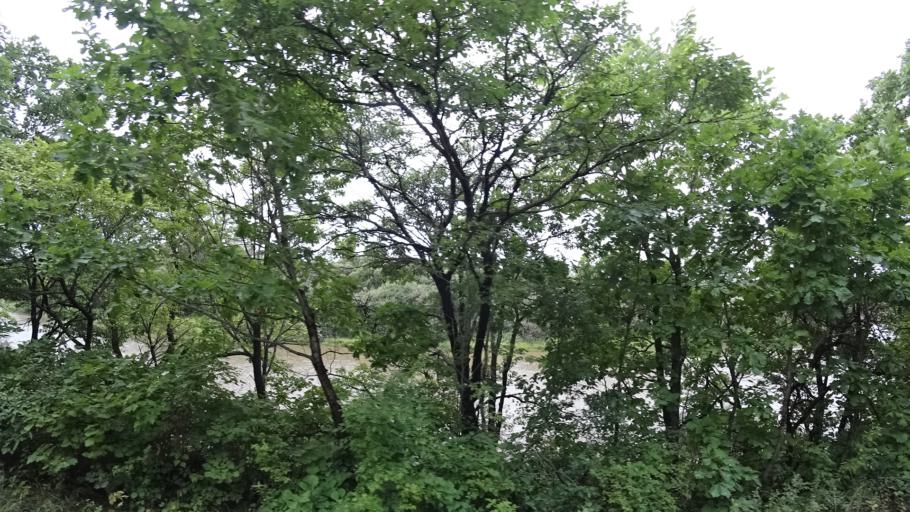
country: RU
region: Primorskiy
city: Monastyrishche
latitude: 44.2745
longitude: 132.4056
